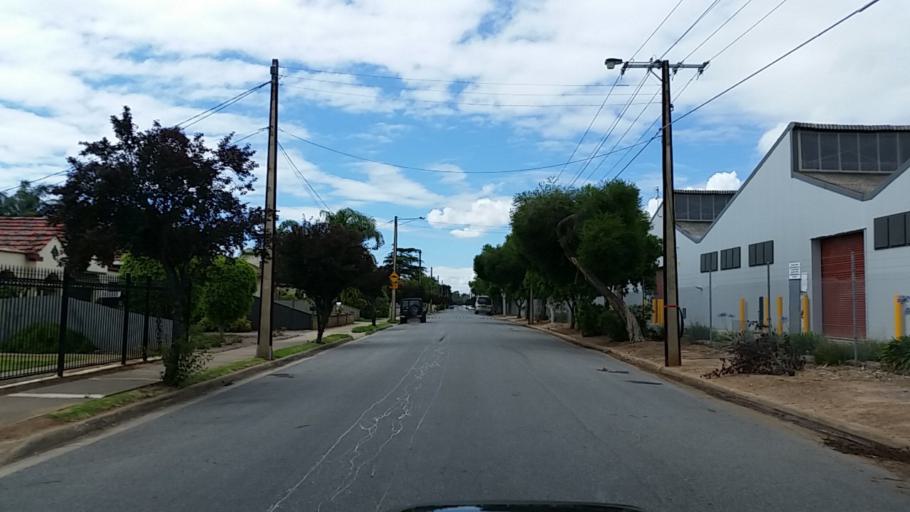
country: AU
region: South Australia
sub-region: Charles Sturt
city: Allenby Gardens
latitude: -34.8989
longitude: 138.5495
